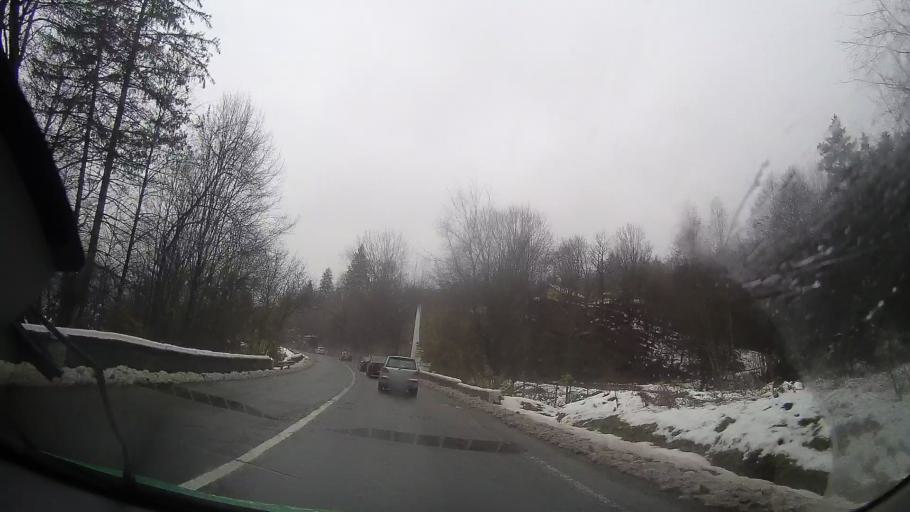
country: RO
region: Neamt
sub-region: Comuna Bicaz
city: Dodeni
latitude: 46.9008
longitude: 26.1182
